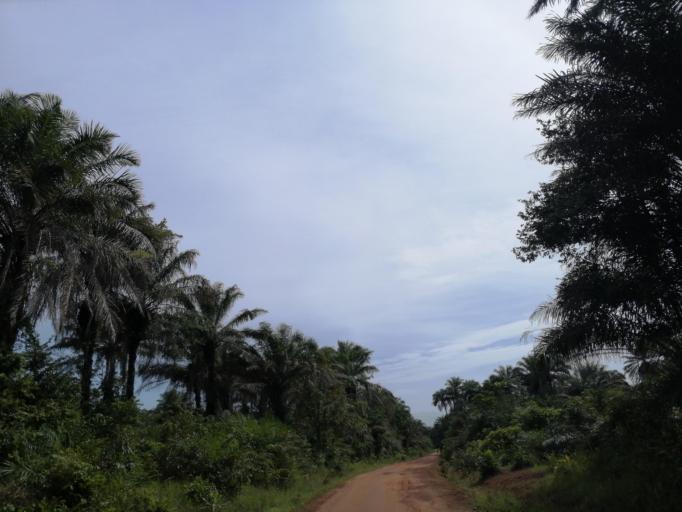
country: SL
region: Northern Province
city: Port Loko
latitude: 8.7901
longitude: -12.9253
